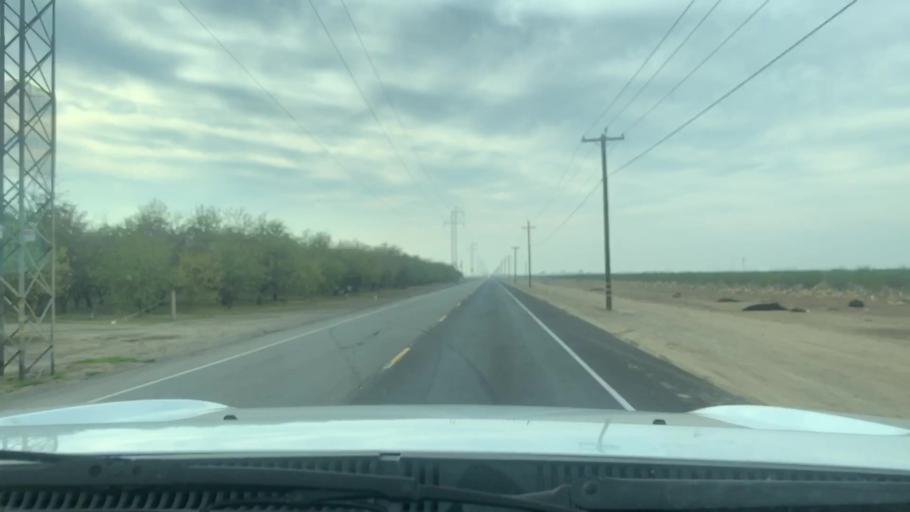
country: US
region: California
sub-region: Kern County
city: Shafter
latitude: 35.4417
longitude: -119.2118
